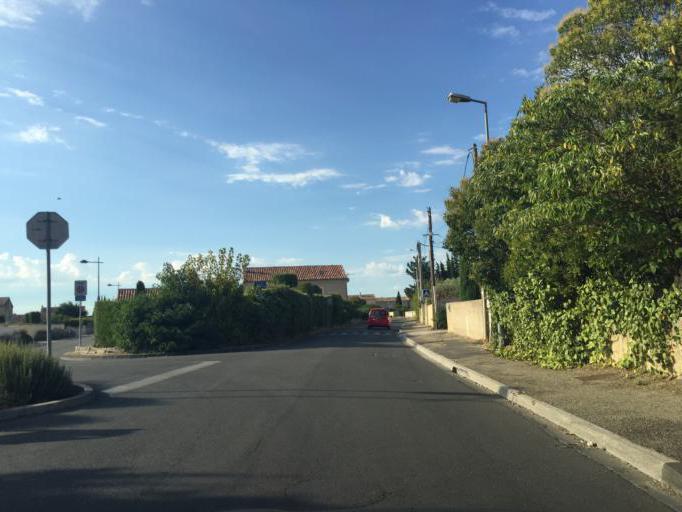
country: FR
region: Provence-Alpes-Cote d'Azur
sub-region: Departement du Vaucluse
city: Pernes-les-Fontaines
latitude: 44.0044
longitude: 5.0563
